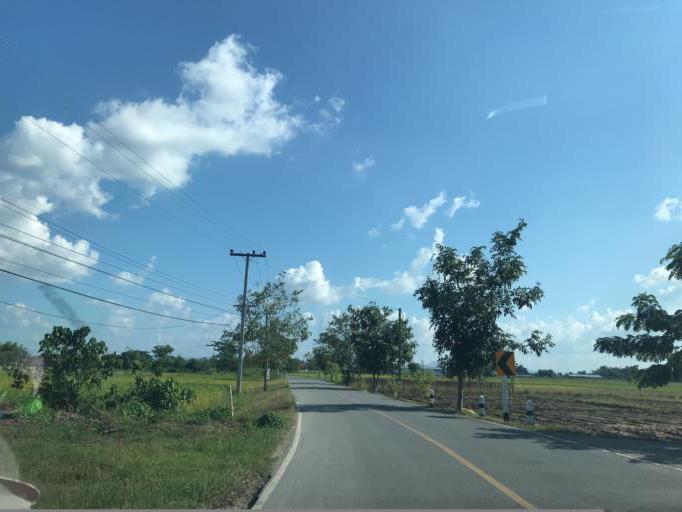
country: TH
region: Chiang Mai
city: Doi Lo
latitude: 18.5402
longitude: 98.8371
